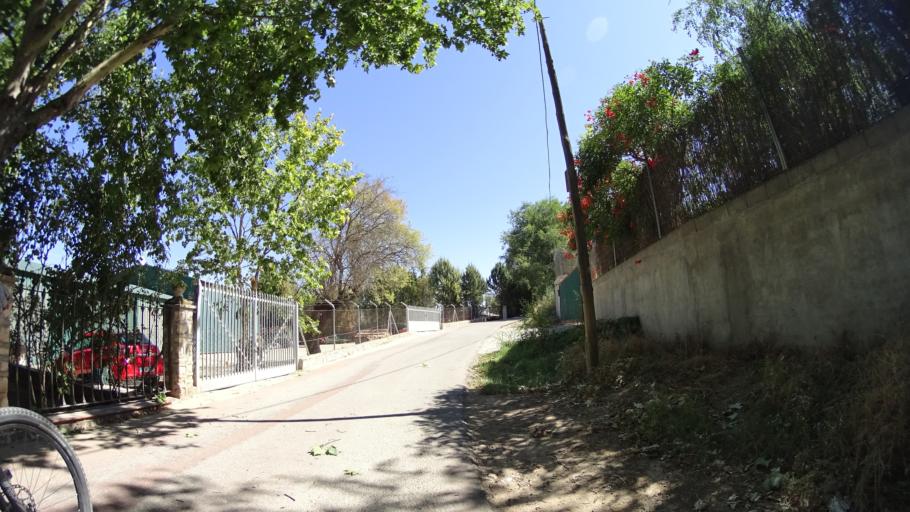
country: ES
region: Madrid
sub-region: Provincia de Madrid
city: Tielmes
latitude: 40.2396
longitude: -3.3103
